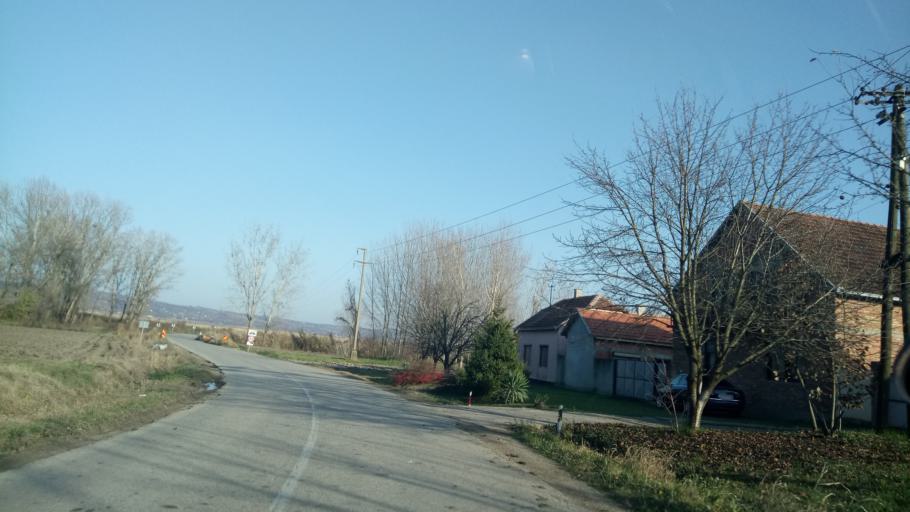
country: RS
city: Krcedin
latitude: 45.1402
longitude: 20.1394
